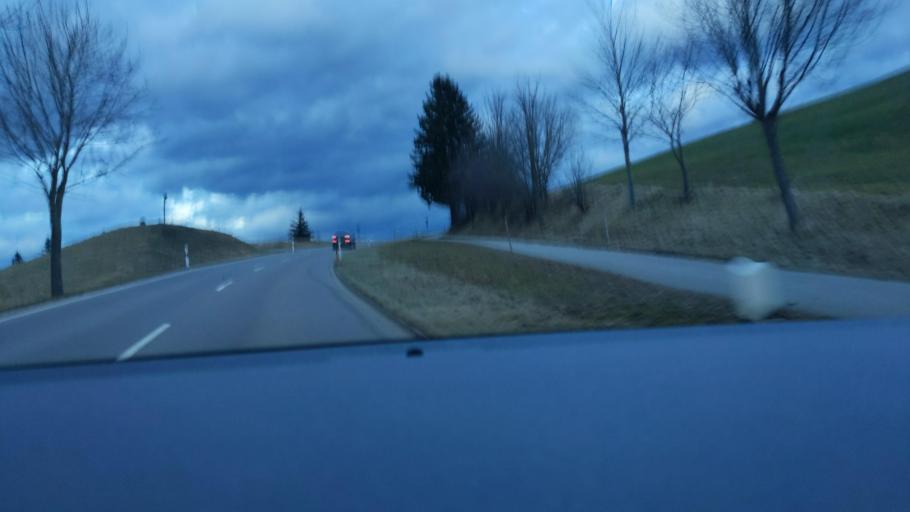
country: DE
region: Bavaria
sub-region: Swabia
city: Pfronten
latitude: 47.5877
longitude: 10.5686
